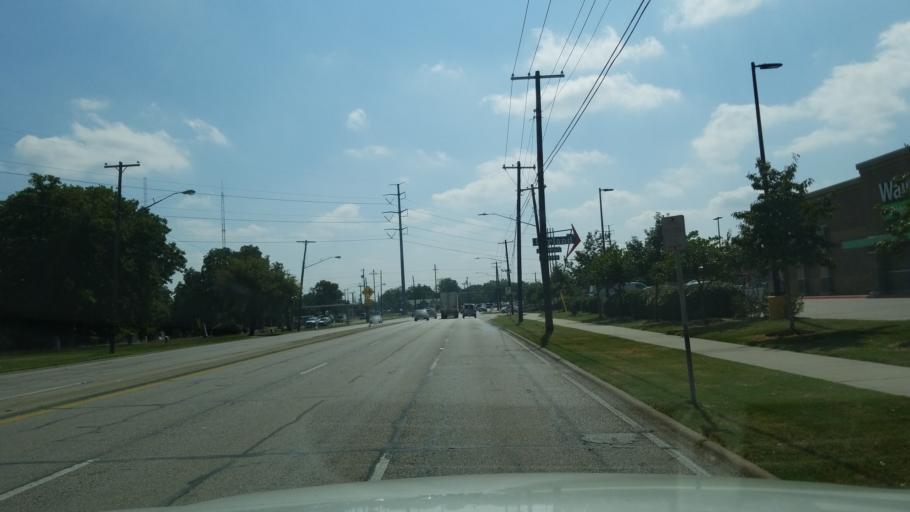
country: US
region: Texas
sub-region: Dallas County
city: Garland
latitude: 32.8969
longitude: -96.6489
